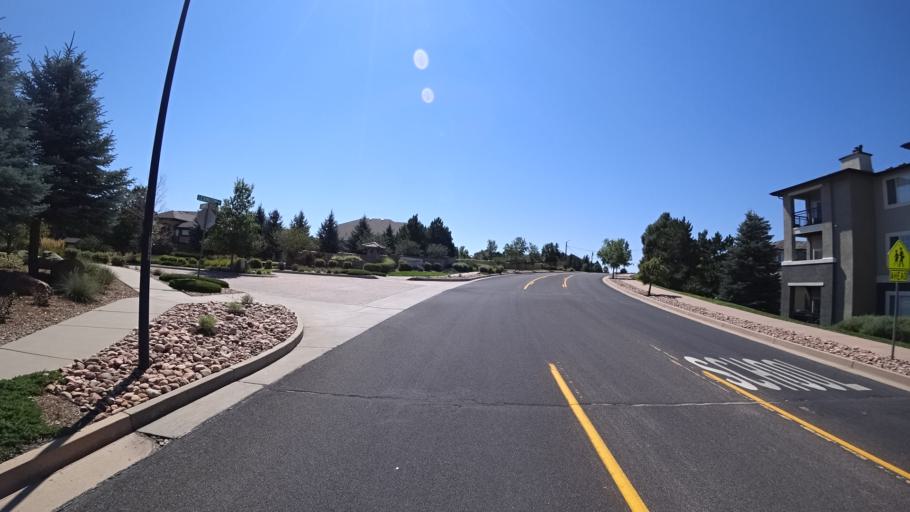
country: US
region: Colorado
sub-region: El Paso County
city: Black Forest
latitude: 38.9688
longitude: -104.7776
